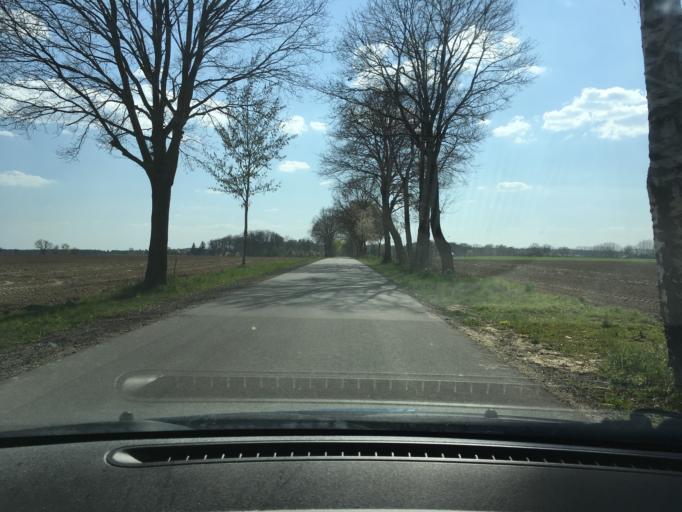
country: DE
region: Lower Saxony
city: Reinstorf
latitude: 53.2094
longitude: 10.5853
